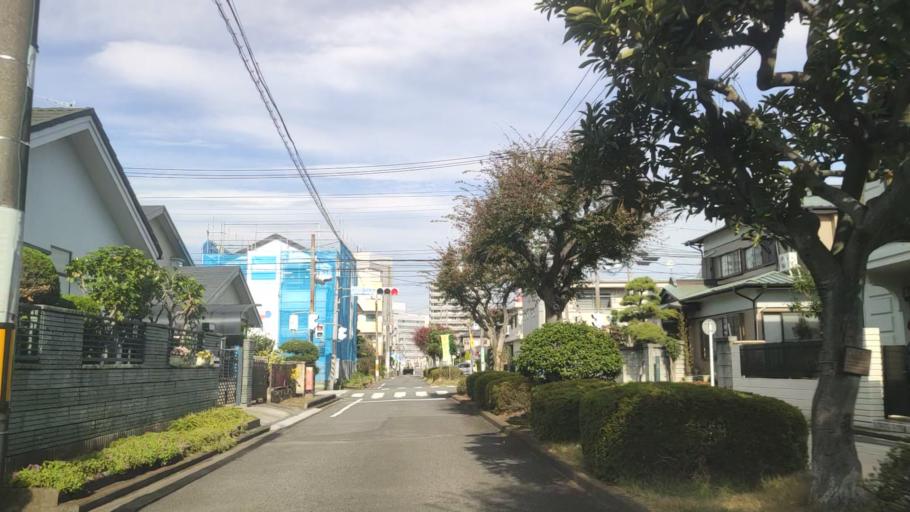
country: JP
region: Kanagawa
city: Atsugi
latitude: 35.4346
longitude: 139.3641
